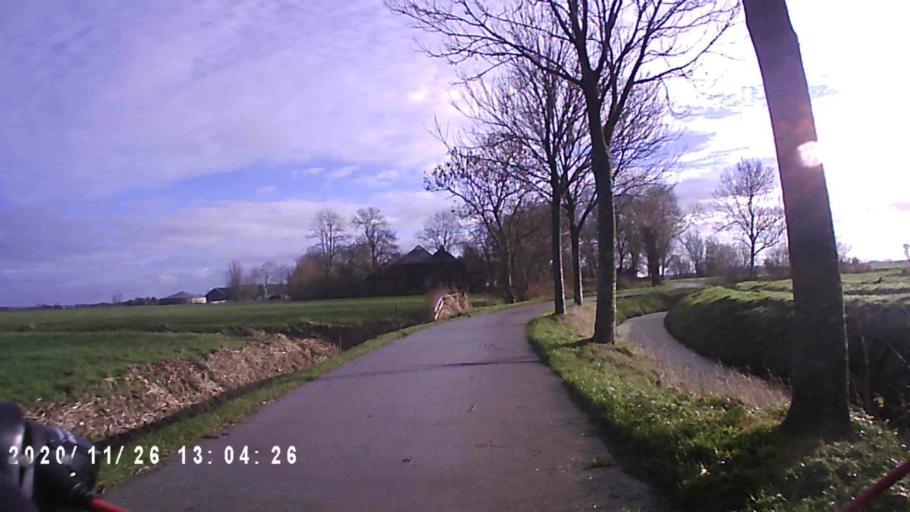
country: NL
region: Groningen
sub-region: Gemeente Appingedam
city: Appingedam
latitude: 53.3534
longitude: 6.8325
